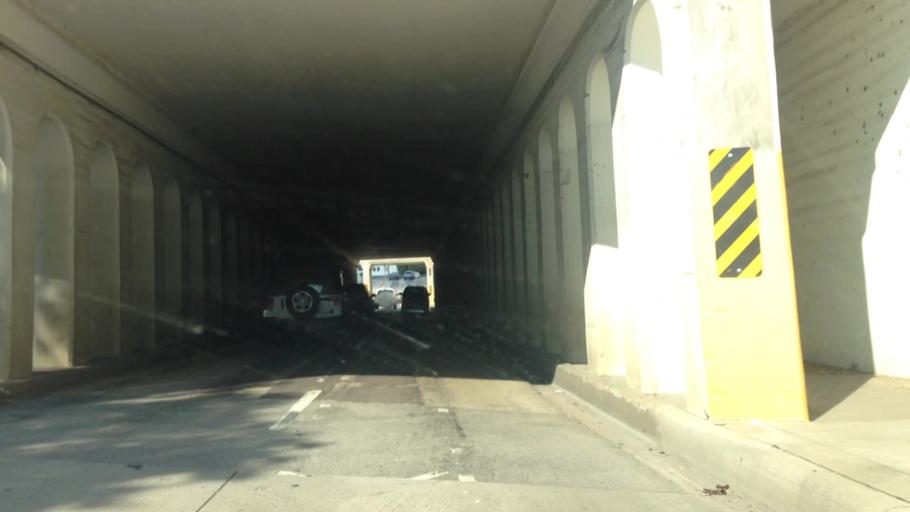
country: US
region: Texas
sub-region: Dallas County
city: Dallas
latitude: 32.7690
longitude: -96.8011
